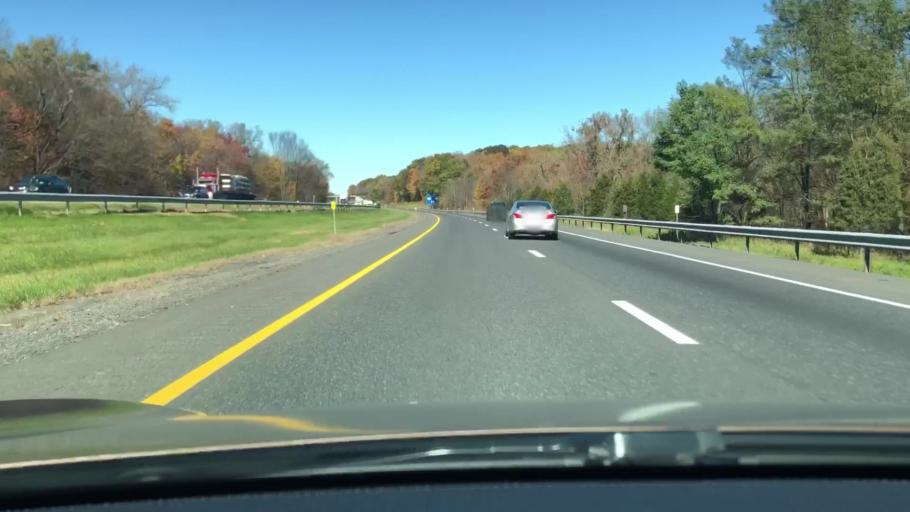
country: US
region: New York
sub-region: Orange County
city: Gardnertown
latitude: 41.5550
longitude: -74.0806
